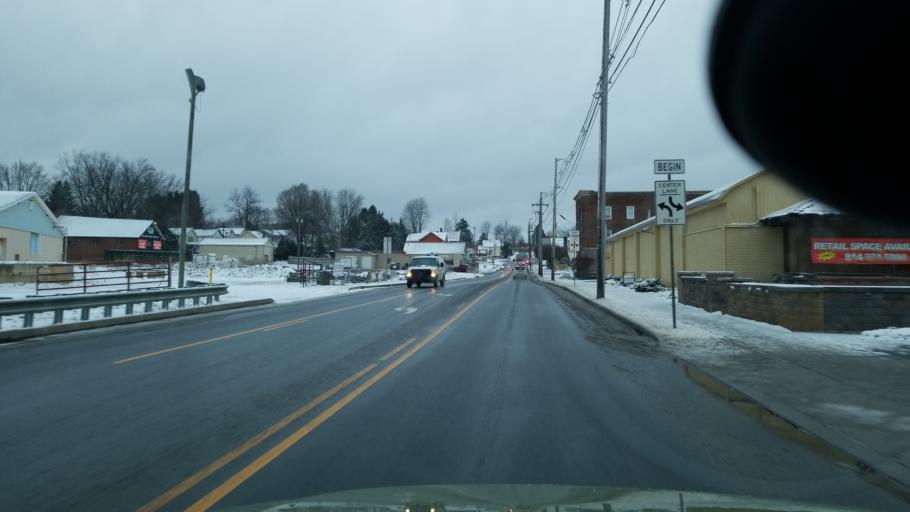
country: US
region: Pennsylvania
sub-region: Clearfield County
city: DuBois
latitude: 41.1263
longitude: -78.7635
